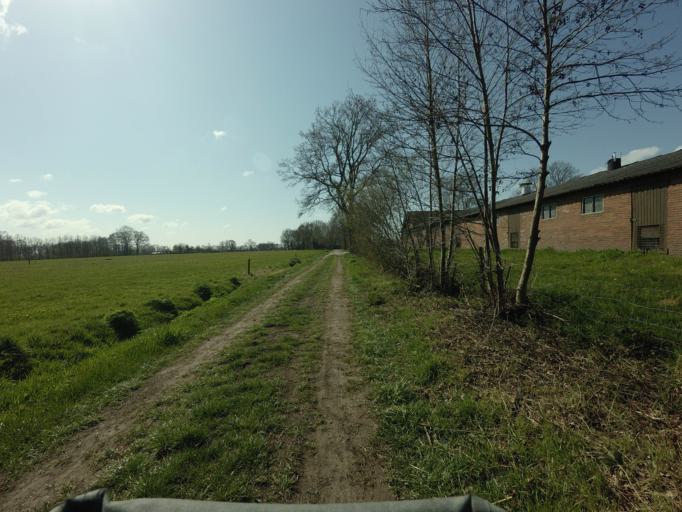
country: NL
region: Gelderland
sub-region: Gemeente Barneveld
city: Terschuur
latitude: 52.1387
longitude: 5.5155
